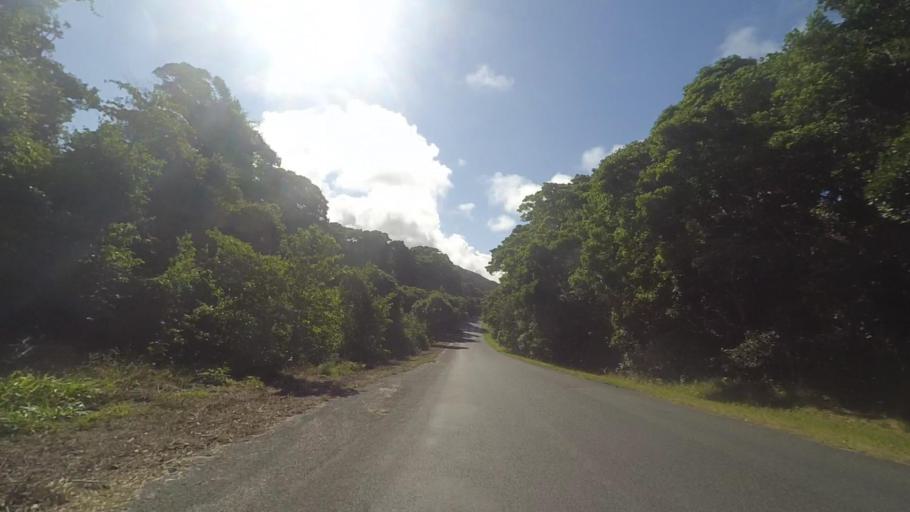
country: AU
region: New South Wales
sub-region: Great Lakes
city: Forster
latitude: -32.4346
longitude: 152.5276
